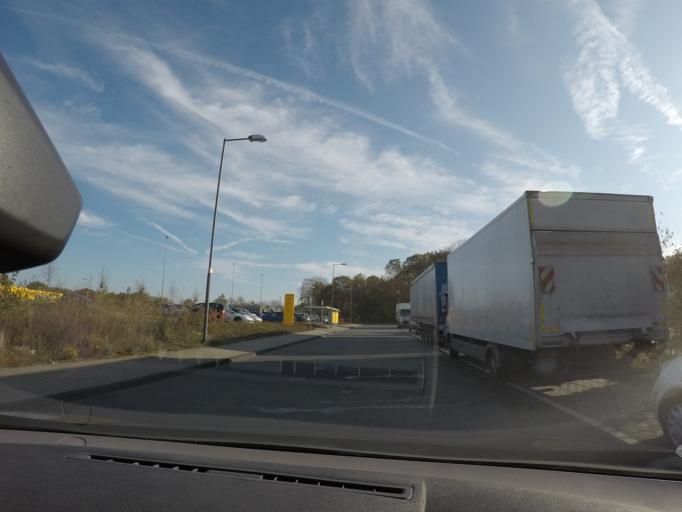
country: DE
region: North Rhine-Westphalia
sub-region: Regierungsbezirk Dusseldorf
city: Wuppertal
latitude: 51.2388
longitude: 7.2018
